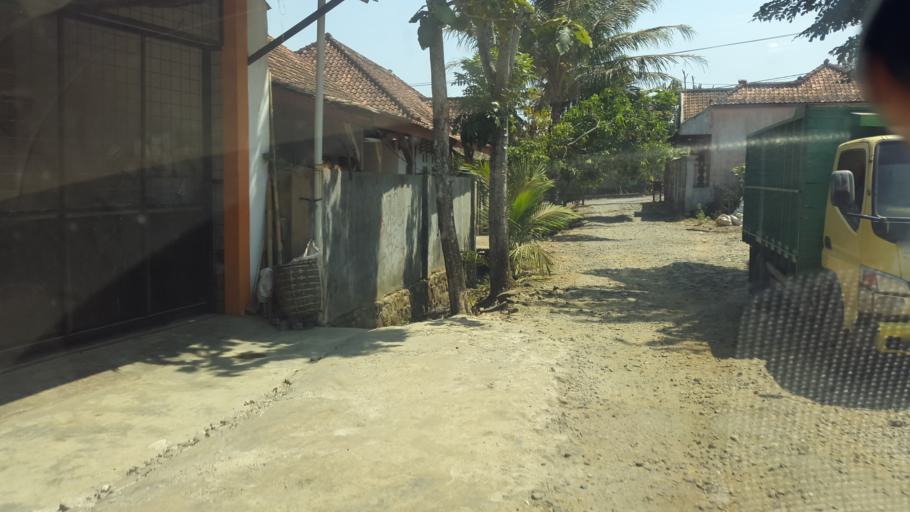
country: ID
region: West Java
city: Ciracap
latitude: -7.3288
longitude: 106.5222
